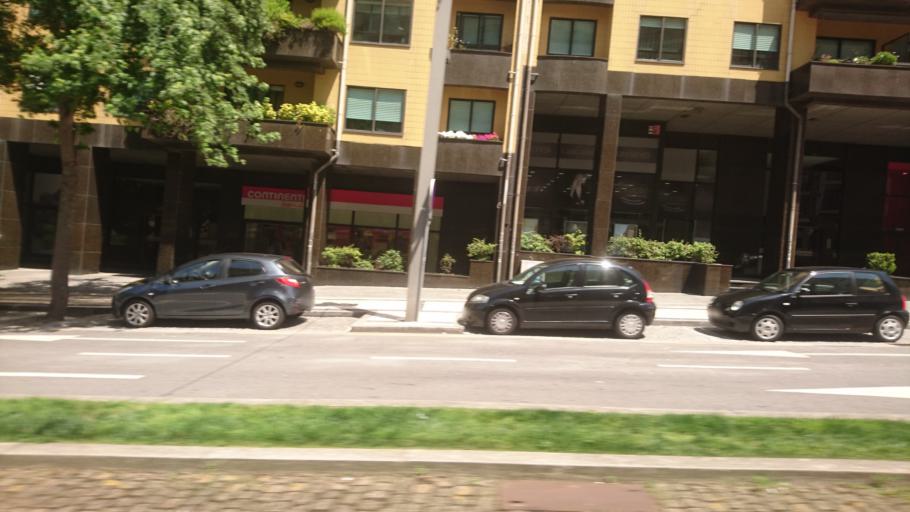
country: PT
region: Porto
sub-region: Vila Nova de Gaia
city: Vila Nova de Gaia
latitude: 41.1217
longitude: -8.6060
